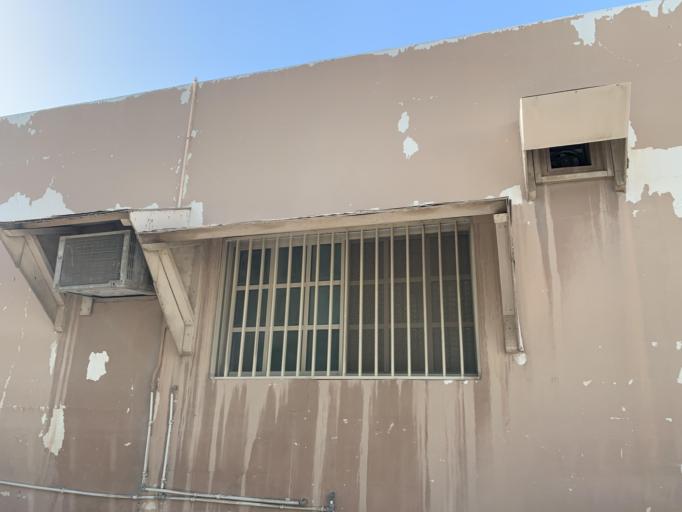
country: BH
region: Muharraq
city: Al Muharraq
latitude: 26.2640
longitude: 50.6045
